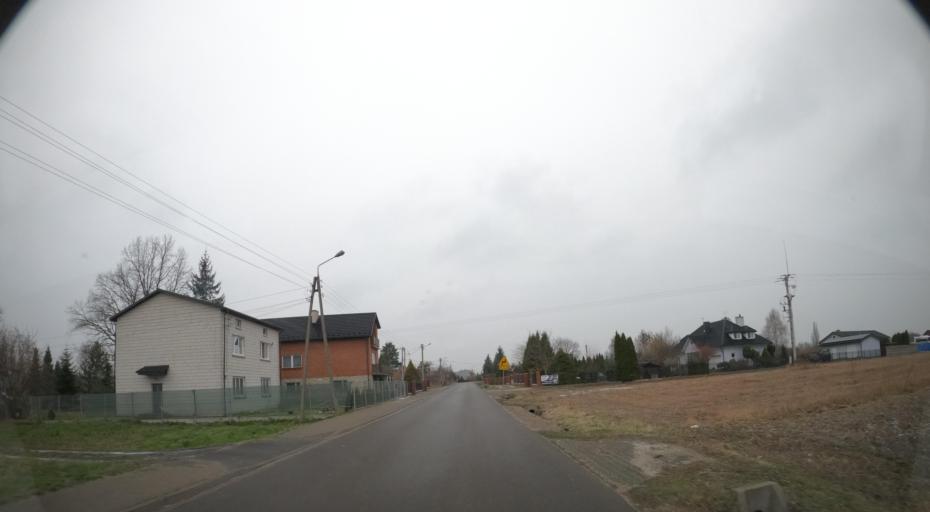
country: PL
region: Masovian Voivodeship
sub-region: Powiat radomski
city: Skaryszew
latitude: 51.3796
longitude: 21.2348
